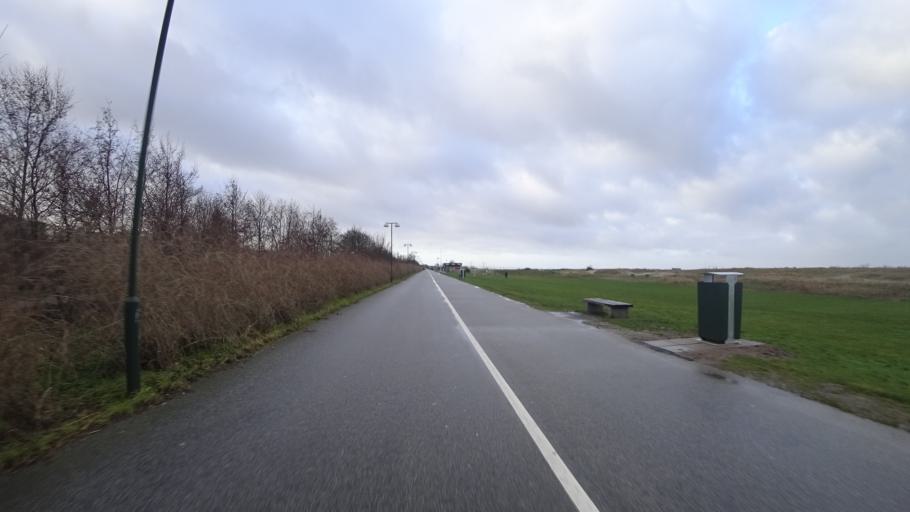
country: SE
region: Skane
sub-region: Malmo
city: Malmoe
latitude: 55.6018
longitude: 12.9656
